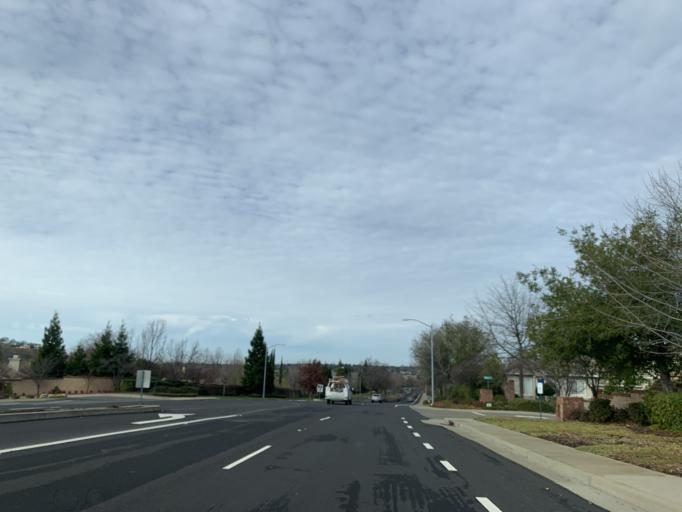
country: US
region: California
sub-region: El Dorado County
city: El Dorado Hills
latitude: 38.6729
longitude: -121.1016
